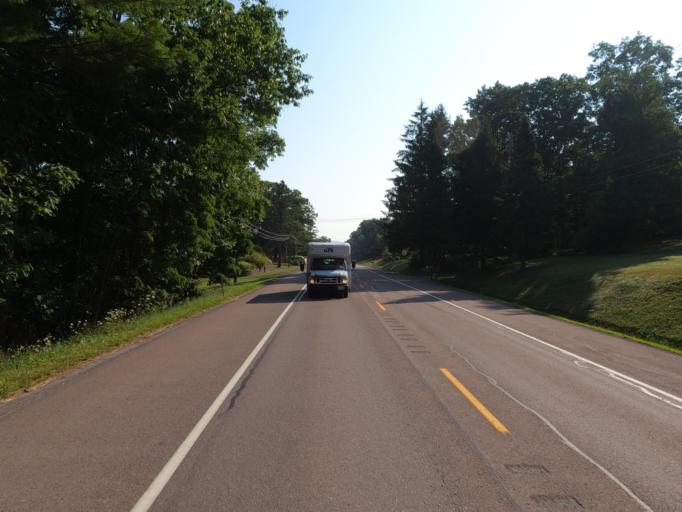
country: US
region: Maryland
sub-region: Garrett County
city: Mountain Lake Park
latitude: 39.4964
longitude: -79.3378
